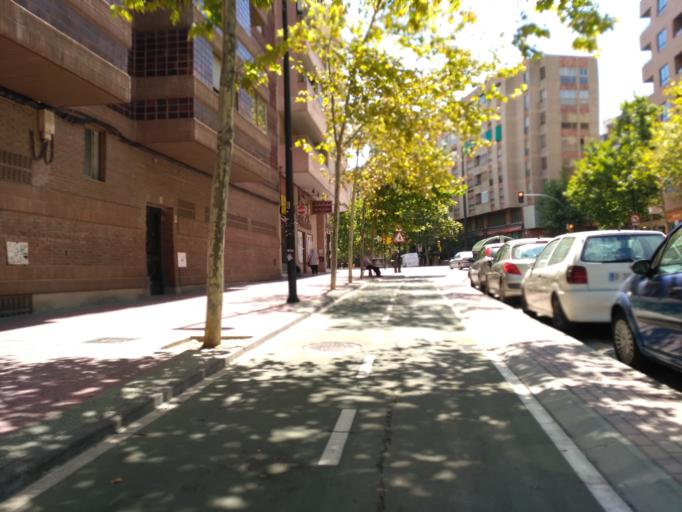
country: ES
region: Aragon
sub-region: Provincia de Zaragoza
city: Delicias
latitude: 41.6541
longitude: -0.9045
